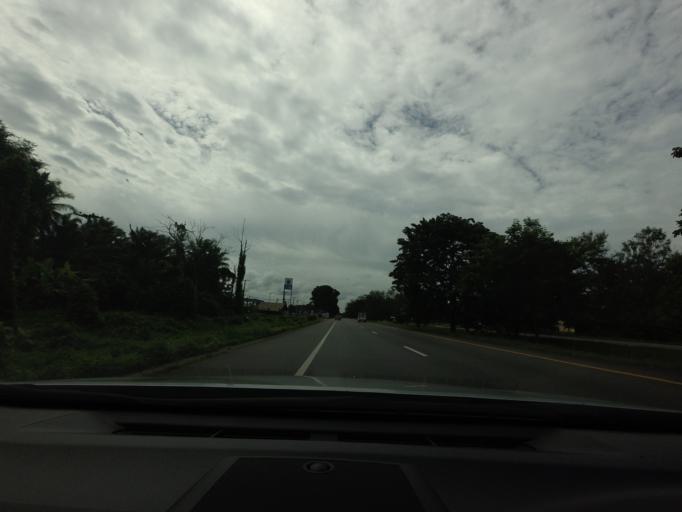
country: TH
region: Chumphon
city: Lamae
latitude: 9.7329
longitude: 99.1024
